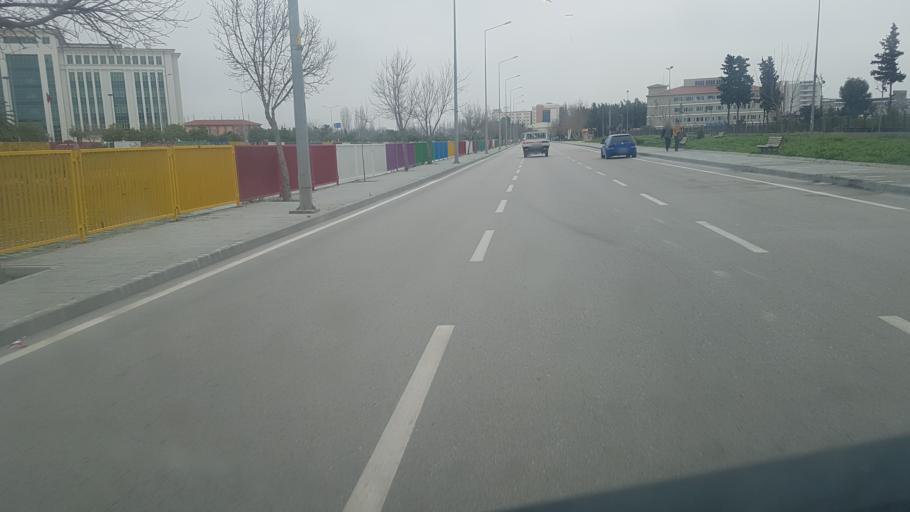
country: TR
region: Adana
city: Adana
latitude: 37.0131
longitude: 35.3450
